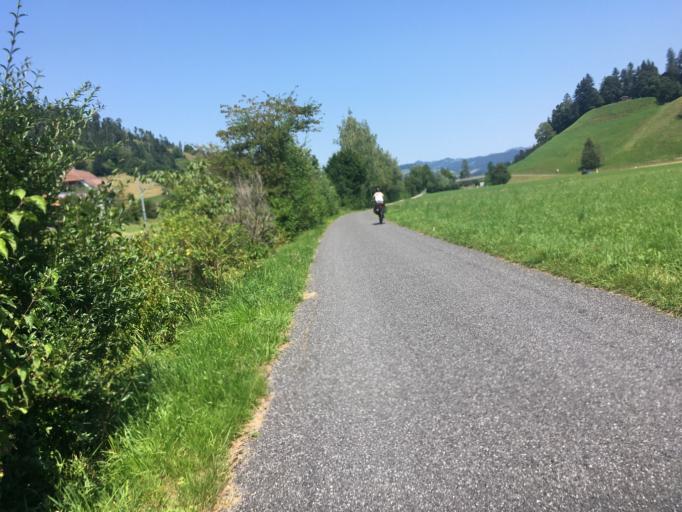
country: CH
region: Bern
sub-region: Emmental District
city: Signau
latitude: 46.9104
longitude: 7.7154
